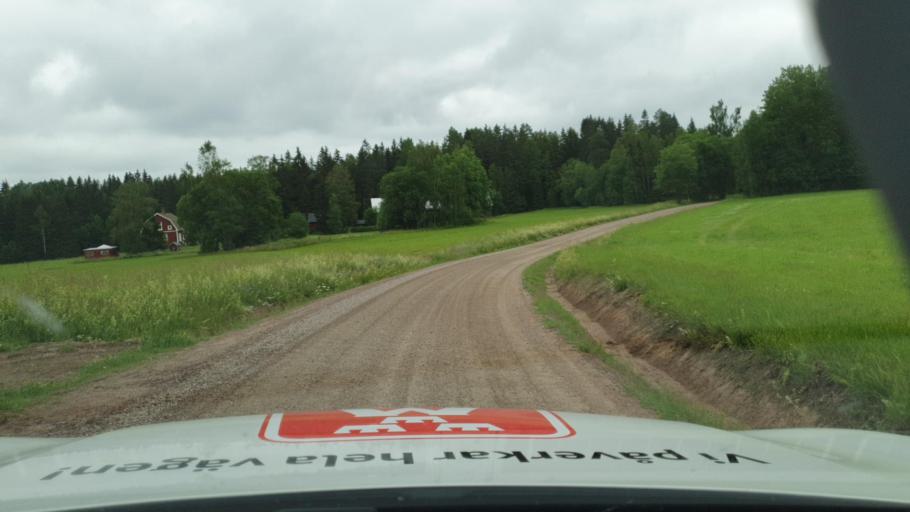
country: SE
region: Vaermland
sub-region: Kristinehamns Kommun
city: Kristinehamn
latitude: 59.5336
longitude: 13.9654
